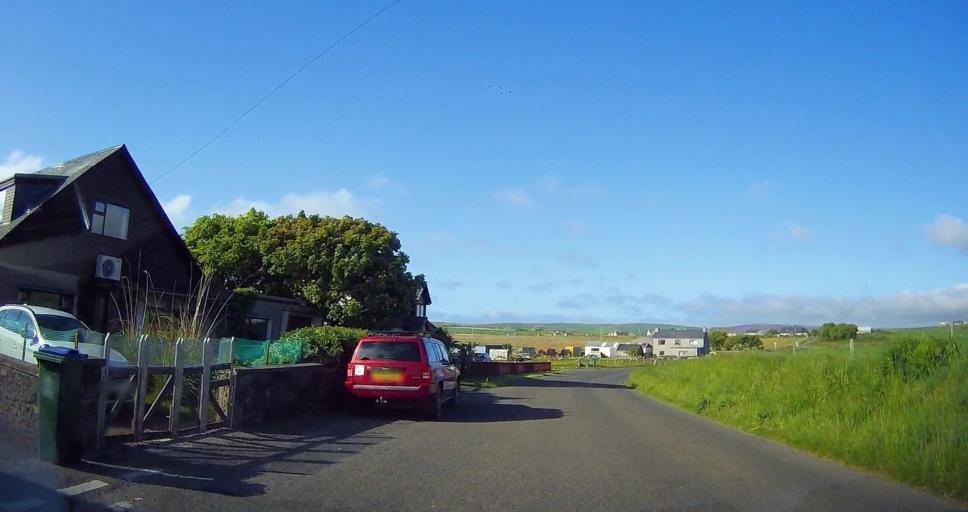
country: GB
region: Scotland
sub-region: Orkney Islands
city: Stromness
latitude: 59.0707
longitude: -3.2270
